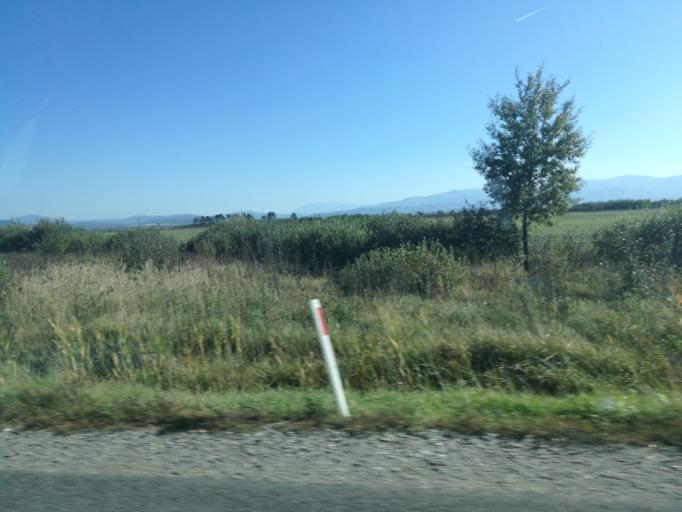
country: RO
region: Brasov
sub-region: Comuna Sercaia
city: Sercaia
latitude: 45.8287
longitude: 25.1165
